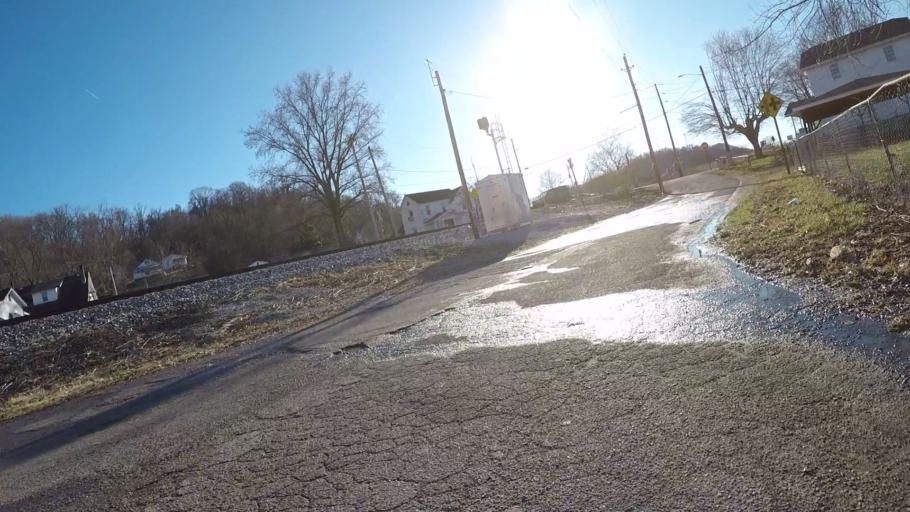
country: US
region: West Virginia
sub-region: Cabell County
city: Huntington
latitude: 38.4274
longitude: -82.3821
